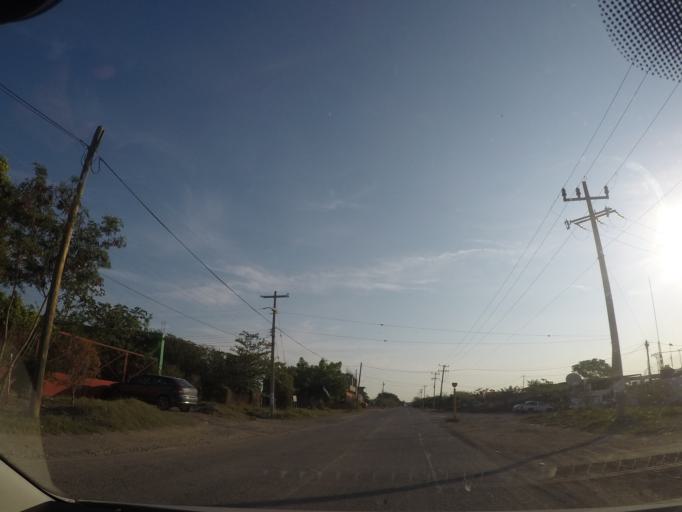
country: MX
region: Oaxaca
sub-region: Salina Cruz
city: Salina Cruz
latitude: 16.2222
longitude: -95.1888
